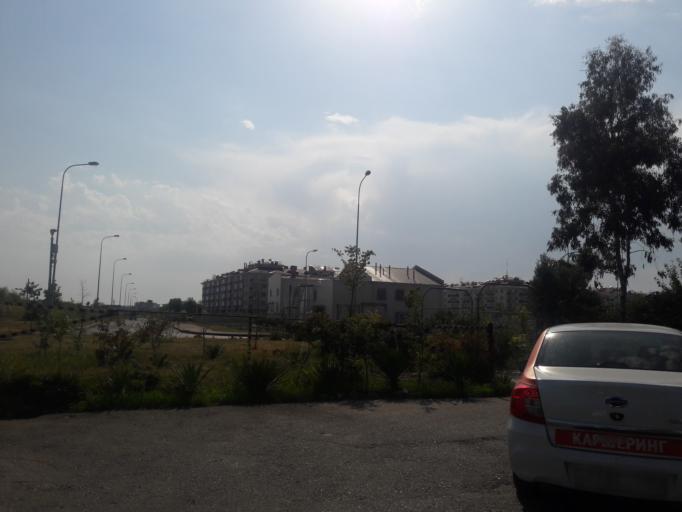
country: RU
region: Krasnodarskiy
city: Vysokoye
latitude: 43.3926
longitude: 40.0009
